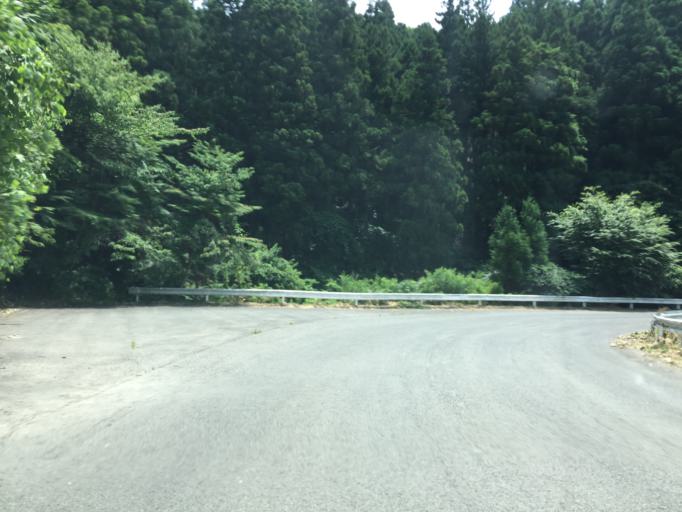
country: JP
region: Fukushima
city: Hobaramachi
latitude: 37.6714
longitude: 140.6563
